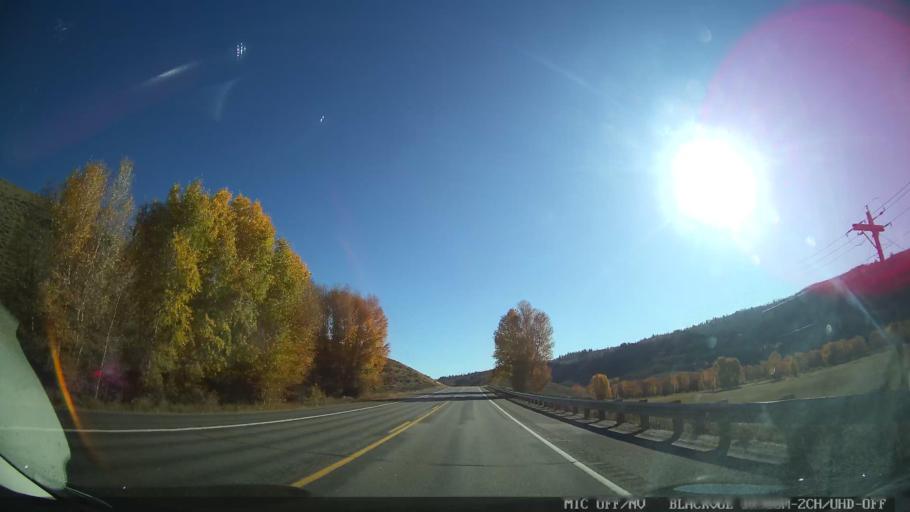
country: US
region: Colorado
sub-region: Grand County
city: Hot Sulphur Springs
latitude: 40.0989
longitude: -106.0371
